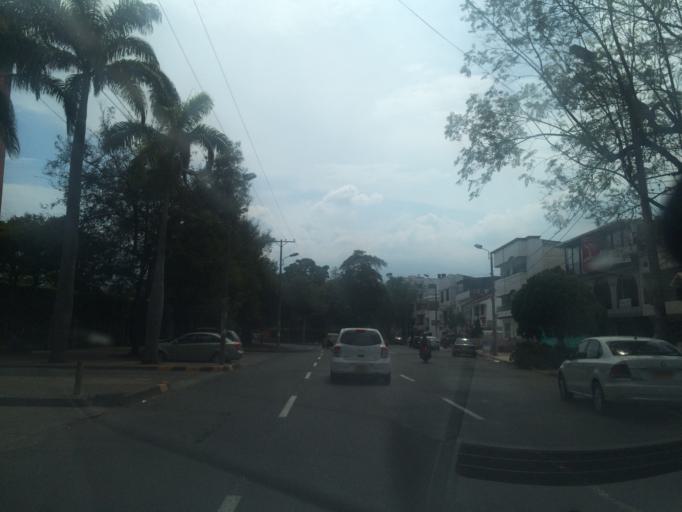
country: CO
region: Valle del Cauca
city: Cali
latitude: 3.3806
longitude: -76.5305
